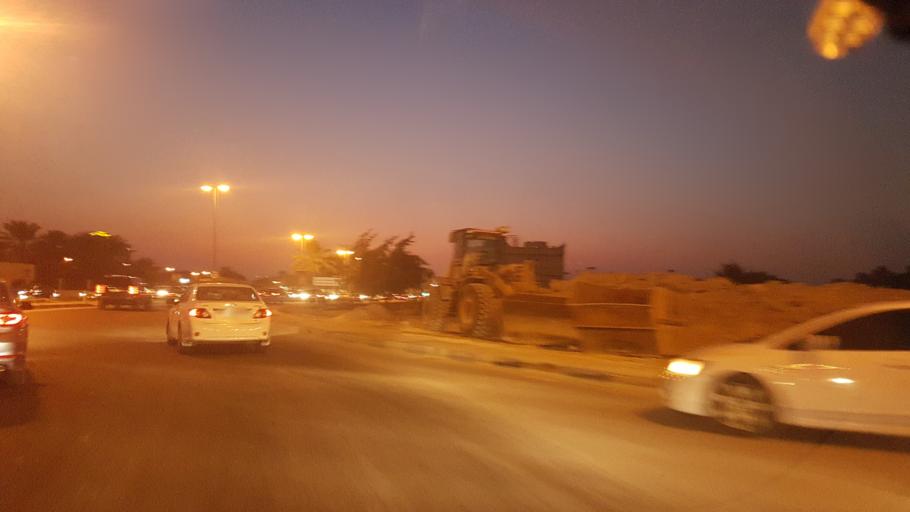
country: BH
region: Manama
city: Jidd Hafs
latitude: 26.2206
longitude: 50.4991
